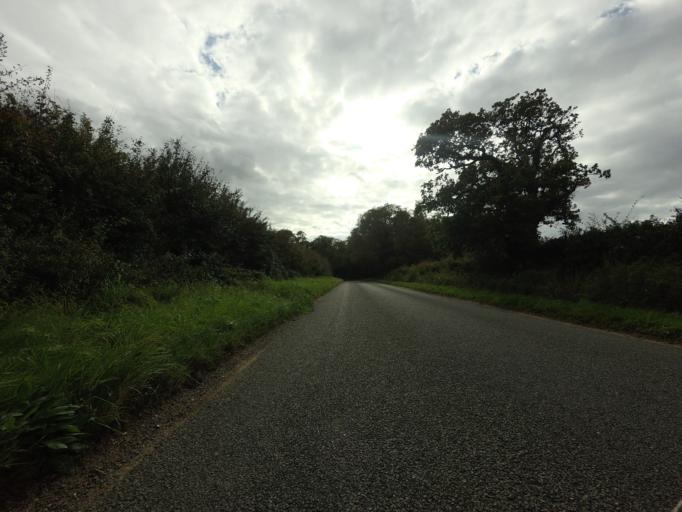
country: GB
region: England
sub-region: Norfolk
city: Snettisham
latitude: 52.8880
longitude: 0.5255
